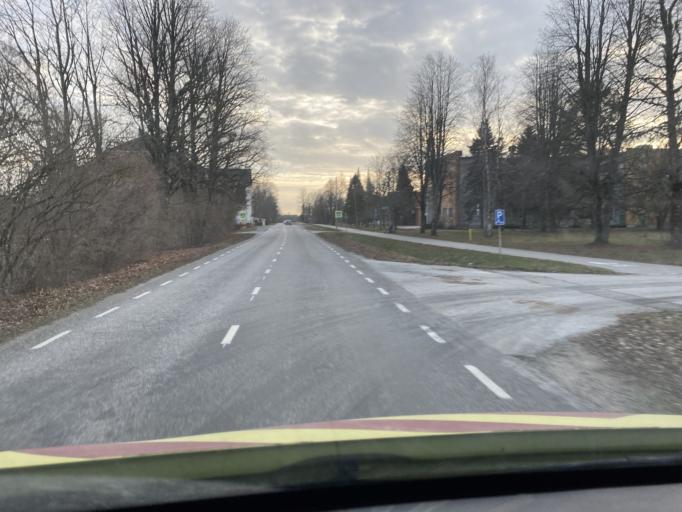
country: EE
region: Jogevamaa
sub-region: Poltsamaa linn
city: Poltsamaa
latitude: 58.6328
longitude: 25.9810
